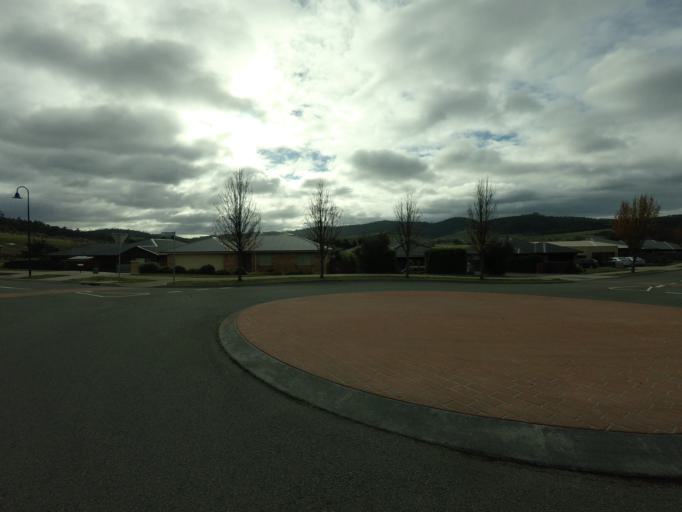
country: AU
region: Tasmania
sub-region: Clarence
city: Howrah
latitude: -42.8835
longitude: 147.4243
